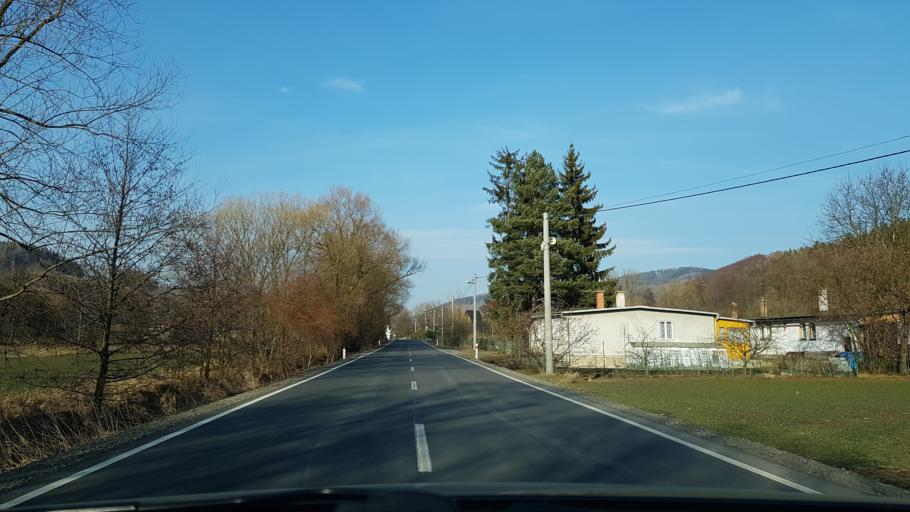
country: CZ
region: Olomoucky
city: Dolni Bohdikov
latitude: 49.9943
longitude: 16.8932
